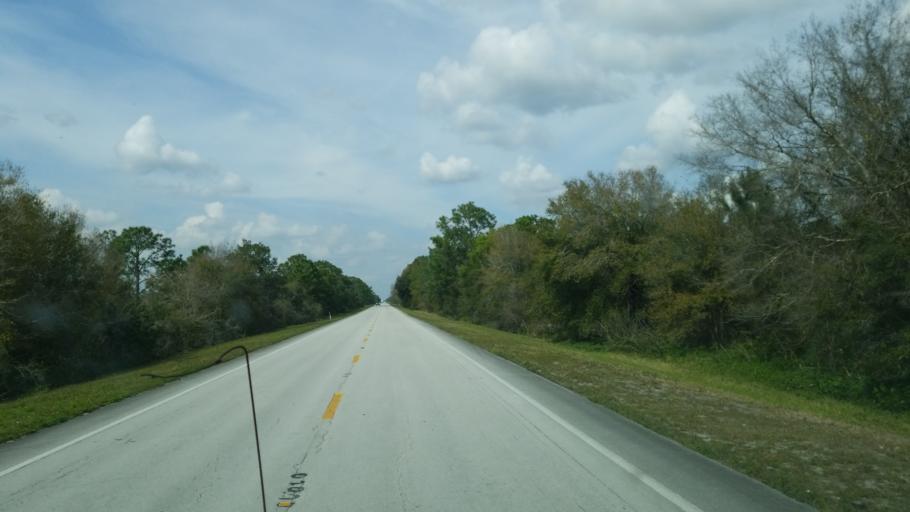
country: US
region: Florida
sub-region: Indian River County
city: Fellsmere
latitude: 27.6461
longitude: -80.8769
